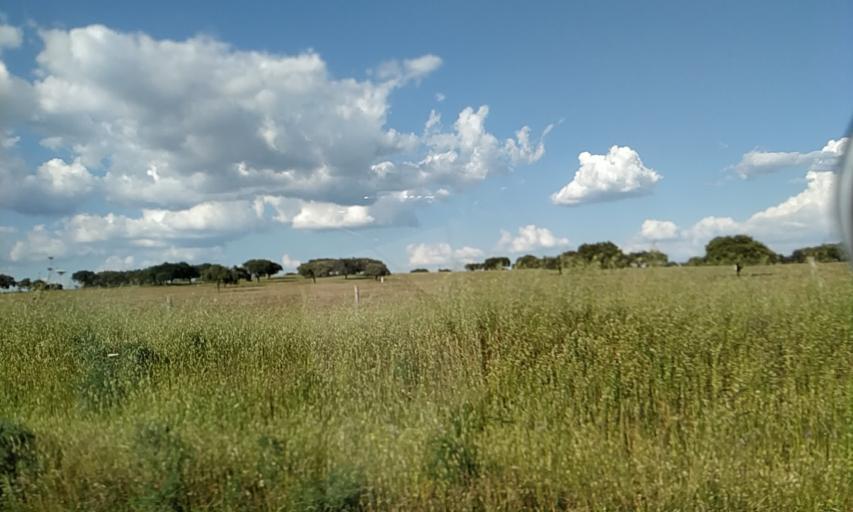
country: PT
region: Portalegre
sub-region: Portalegre
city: Urra
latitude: 39.1488
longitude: -7.4533
